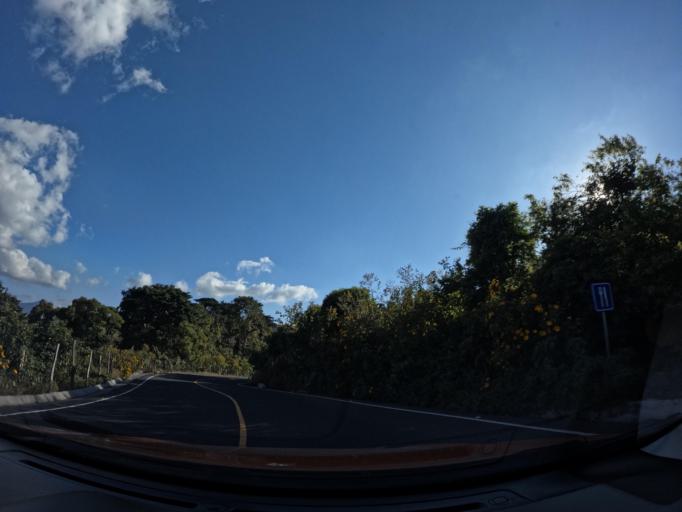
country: GT
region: Escuintla
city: Palin
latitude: 14.4618
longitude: -90.6944
